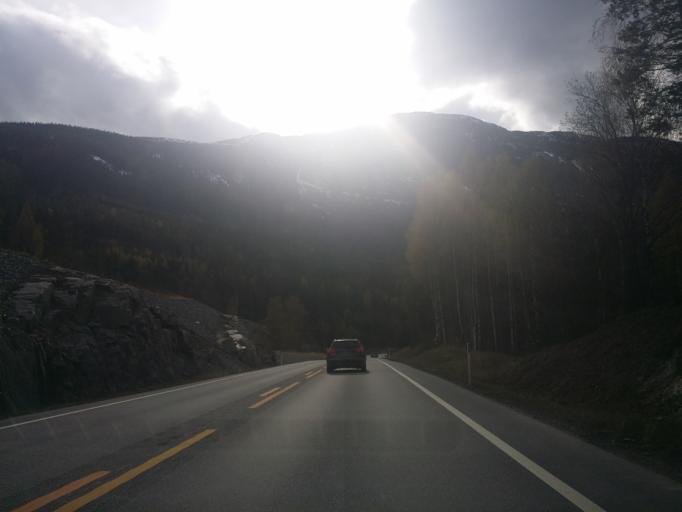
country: NO
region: Buskerud
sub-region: Fla
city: Fla
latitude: 60.4442
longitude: 9.2983
